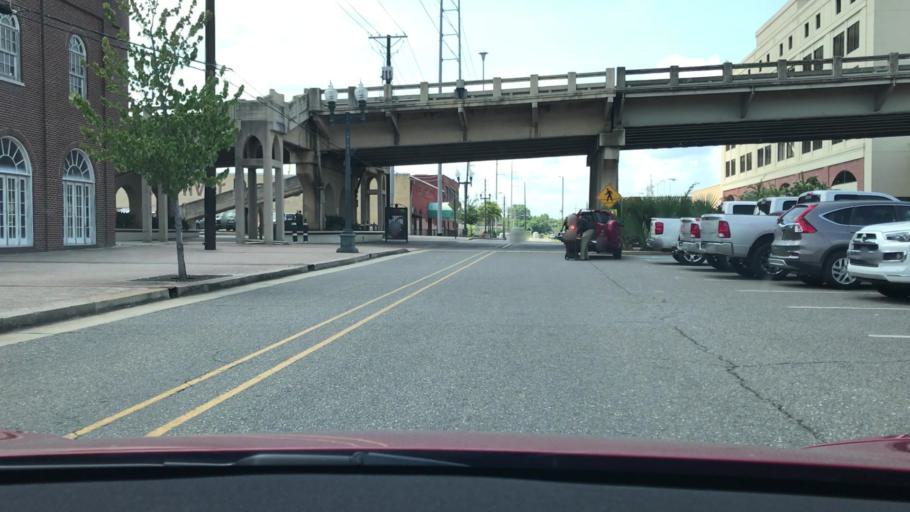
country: US
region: Louisiana
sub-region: Caddo Parish
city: Shreveport
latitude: 32.5153
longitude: -93.7454
